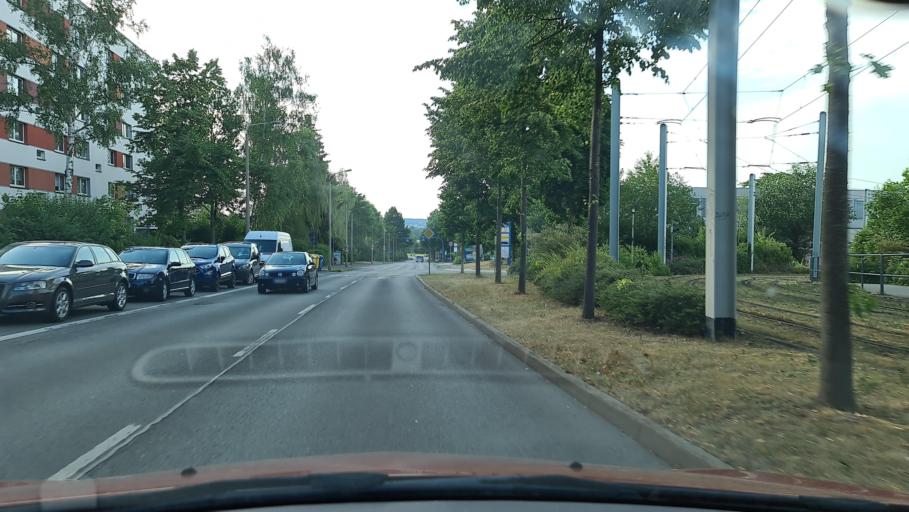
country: DE
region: Saxony
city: Lichtentanne
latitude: 50.6953
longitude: 12.4613
